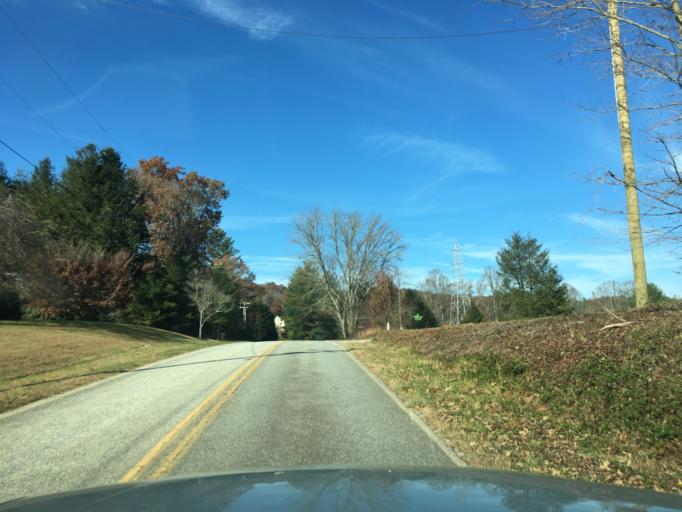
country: US
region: North Carolina
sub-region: Henderson County
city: Etowah
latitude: 35.3295
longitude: -82.6149
